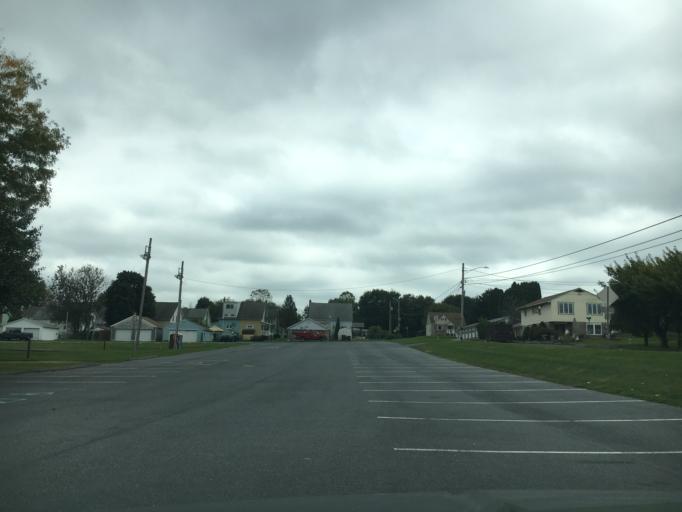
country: US
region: Pennsylvania
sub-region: Lehigh County
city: Cementon
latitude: 40.6839
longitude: -75.5146
